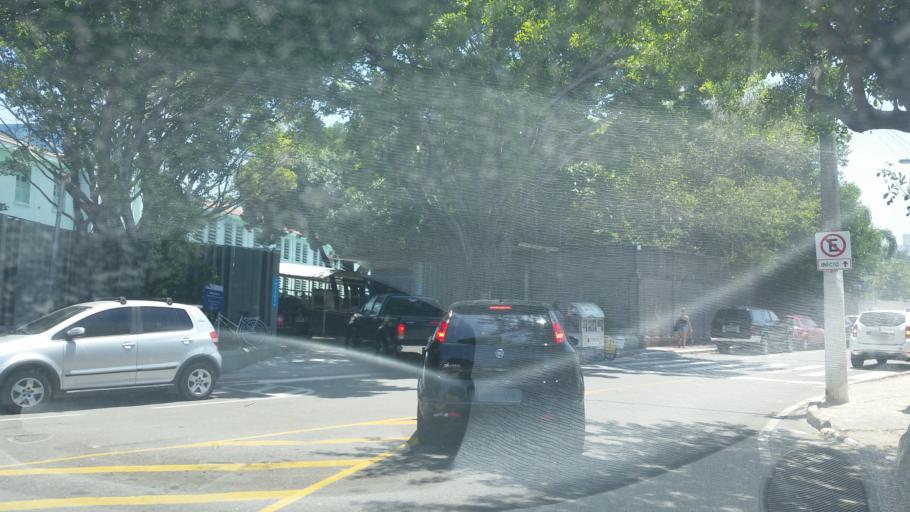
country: BR
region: Espirito Santo
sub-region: Vila Velha
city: Vila Velha
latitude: -20.3375
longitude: -40.2893
